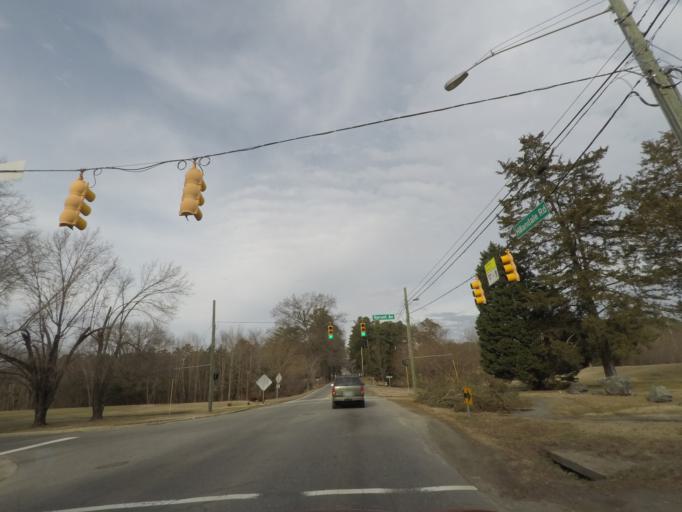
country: US
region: North Carolina
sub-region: Durham County
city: Durham
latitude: 36.0214
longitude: -78.9361
